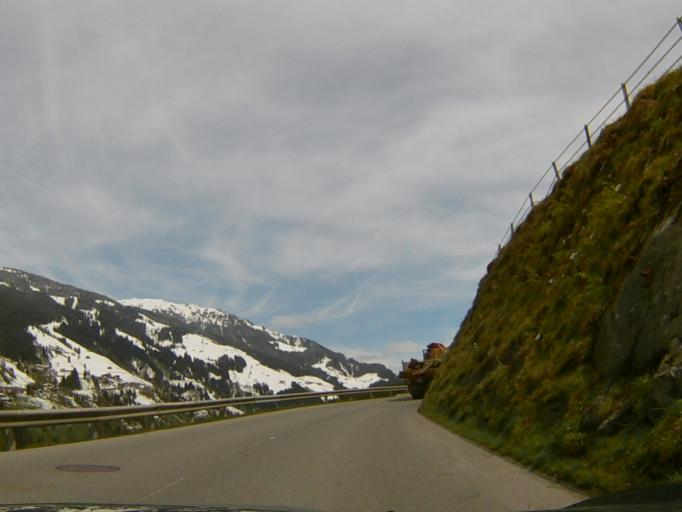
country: AT
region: Tyrol
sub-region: Politischer Bezirk Schwaz
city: Hainzenberg
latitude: 47.2145
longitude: 11.9142
